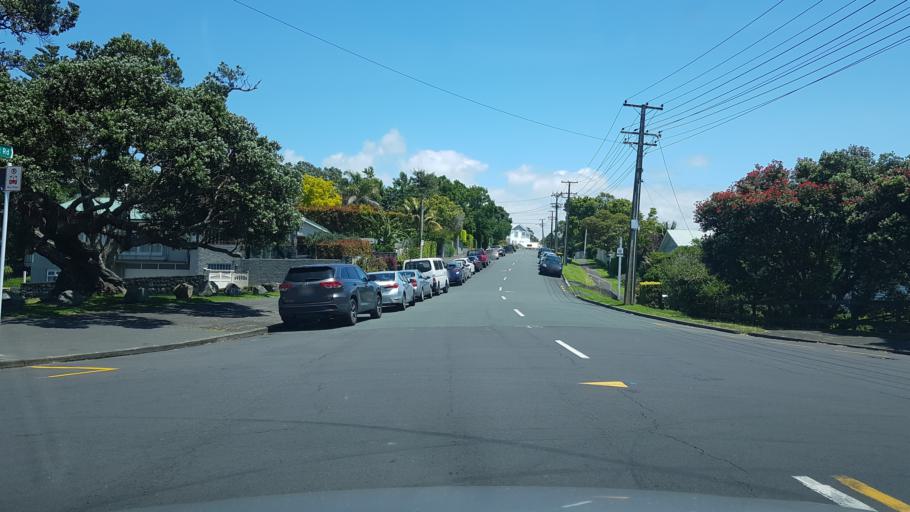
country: NZ
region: Auckland
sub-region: Auckland
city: North Shore
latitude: -36.8265
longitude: 174.7808
